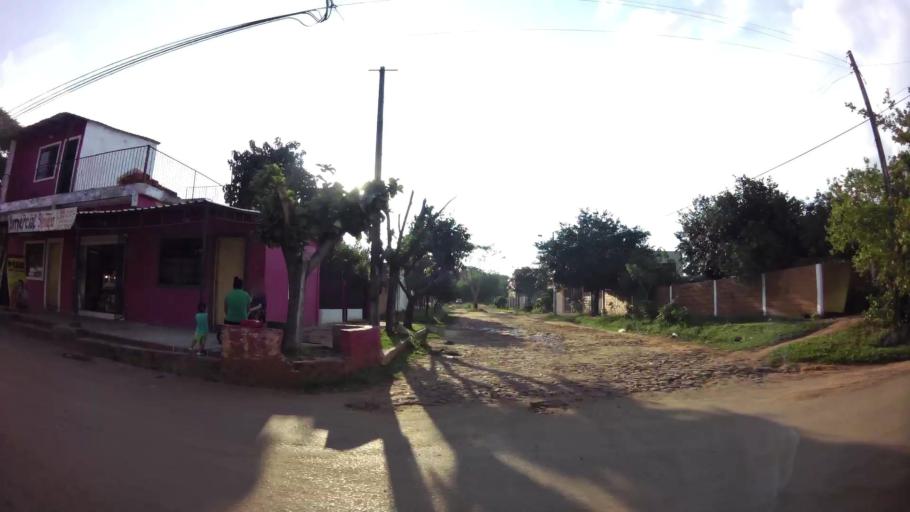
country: PY
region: Central
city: Fernando de la Mora
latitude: -25.3512
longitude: -57.5274
